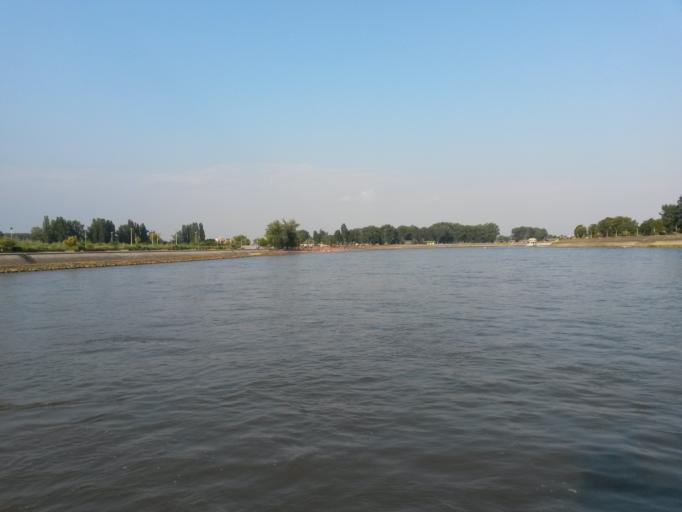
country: HR
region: Osjecko-Baranjska
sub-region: Grad Osijek
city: Osijek
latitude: 45.5637
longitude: 18.6869
